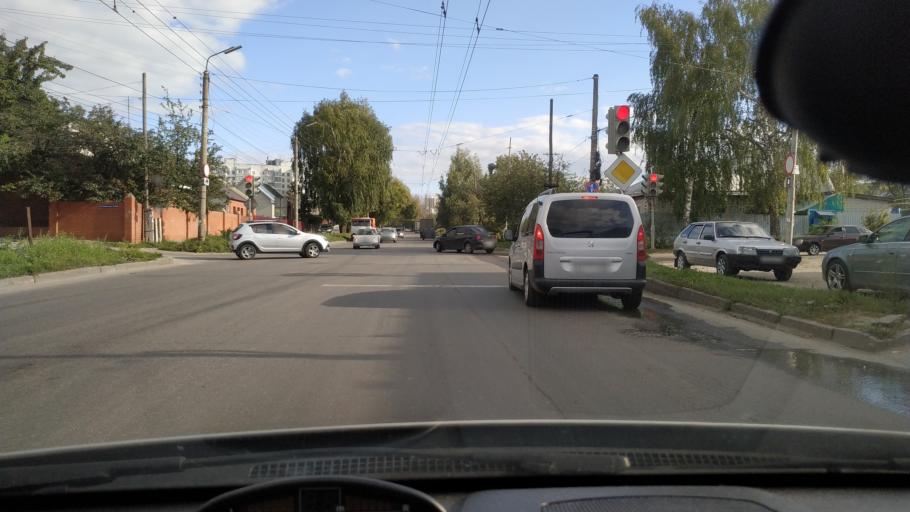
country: RU
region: Rjazan
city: Ryazan'
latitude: 54.6117
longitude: 39.6971
